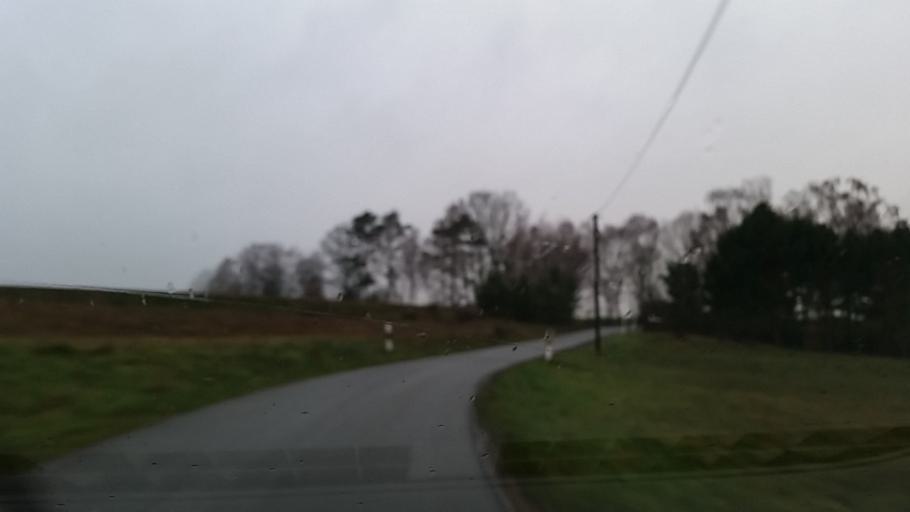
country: DE
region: Brandenburg
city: Gumtow
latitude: 53.0050
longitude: 12.2315
